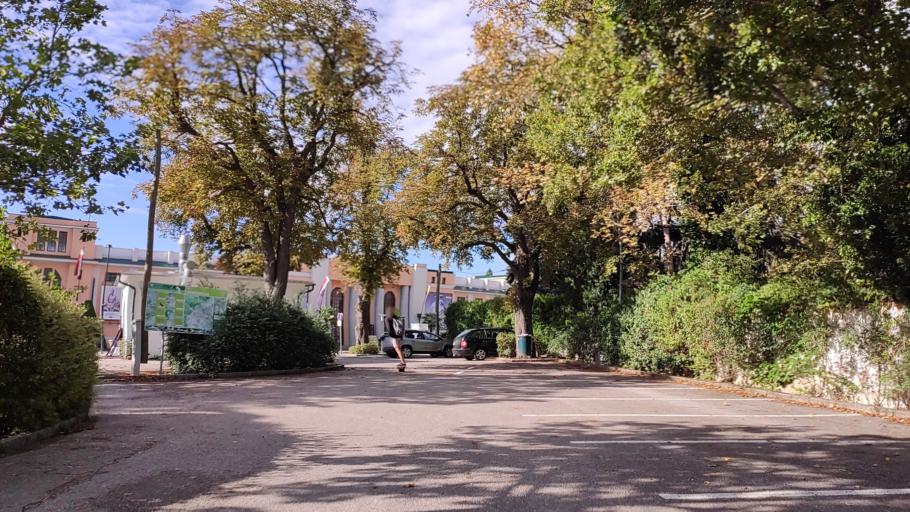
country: AT
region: Lower Austria
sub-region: Politischer Bezirk Baden
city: Baden
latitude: 48.0069
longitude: 16.2193
